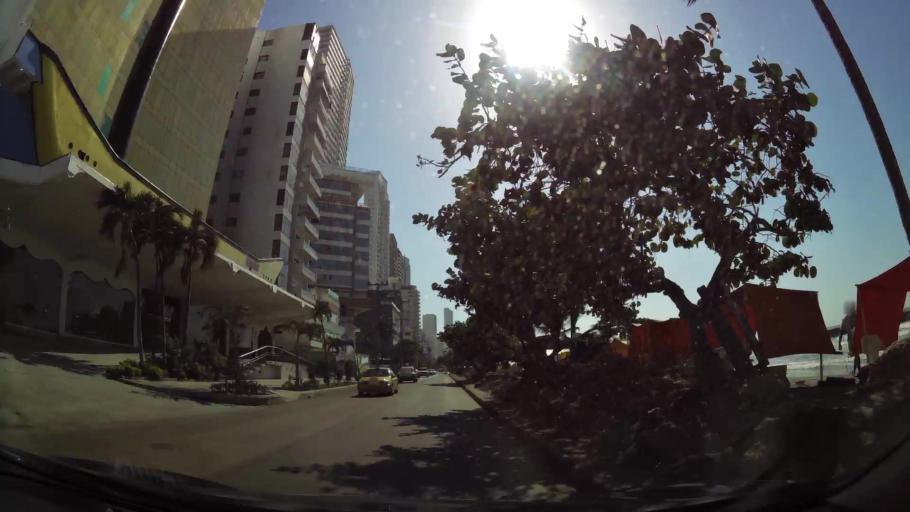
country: CO
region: Bolivar
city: Cartagena
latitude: 10.4067
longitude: -75.5536
